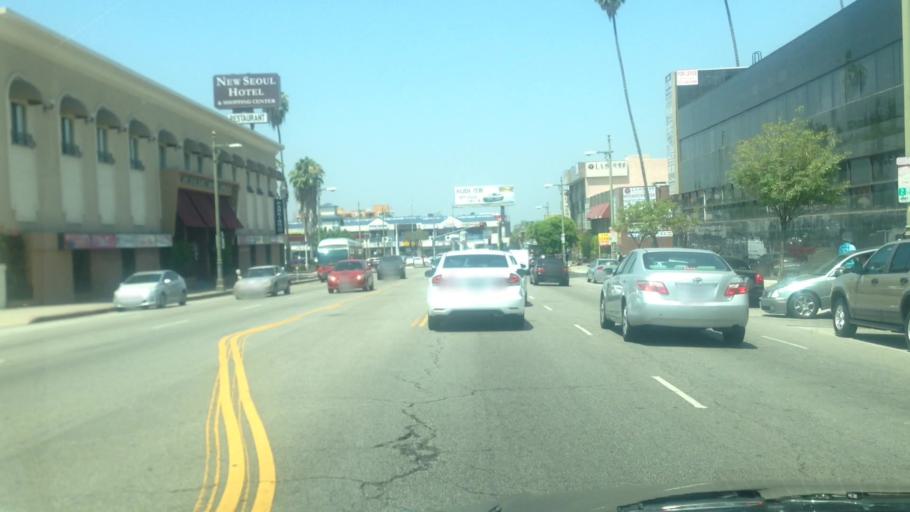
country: US
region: California
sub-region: Los Angeles County
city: Echo Park
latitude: 34.0524
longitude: -118.2895
